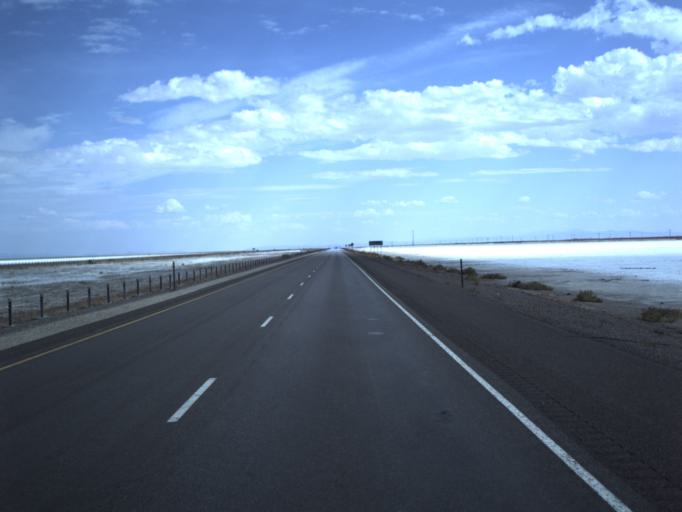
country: US
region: Utah
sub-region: Tooele County
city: Wendover
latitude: 40.7383
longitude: -113.8431
